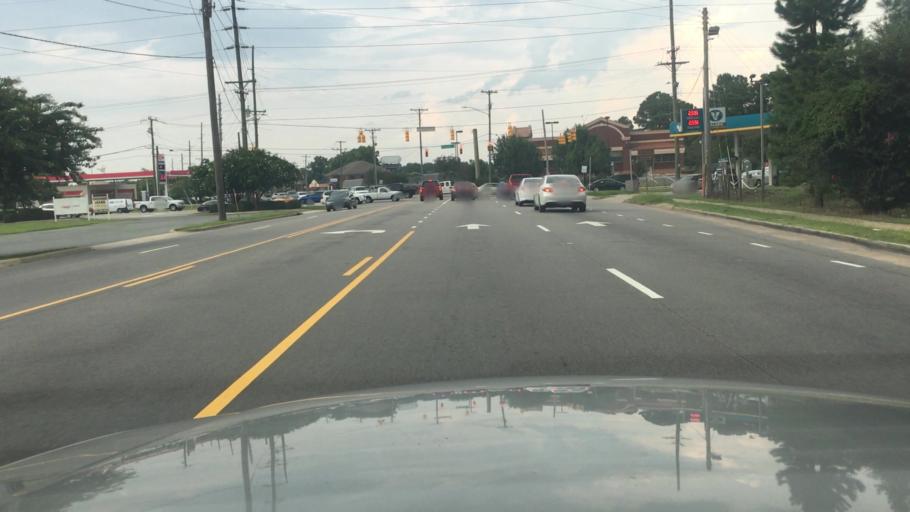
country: US
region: North Carolina
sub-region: Cumberland County
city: Fayetteville
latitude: 35.0663
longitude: -78.9507
